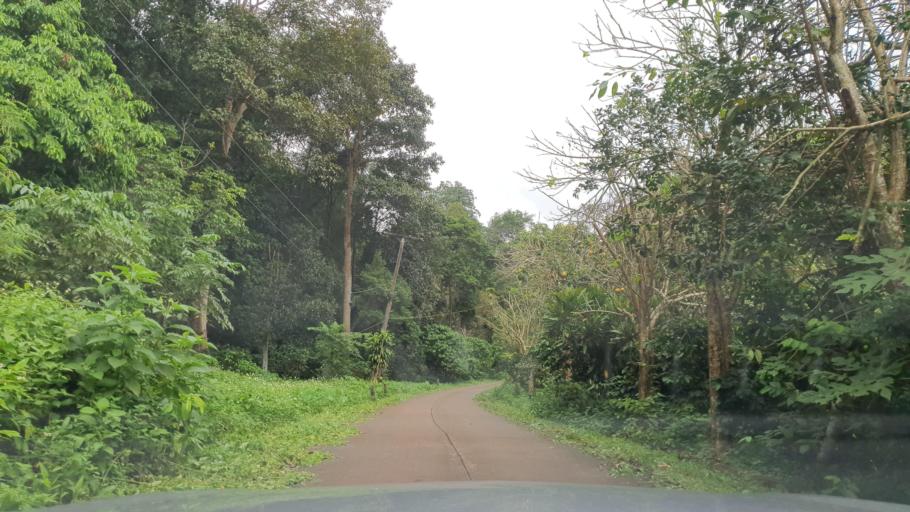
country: TH
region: Chiang Mai
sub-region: Amphoe Chiang Dao
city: Chiang Dao
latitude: 19.2456
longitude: 98.9265
